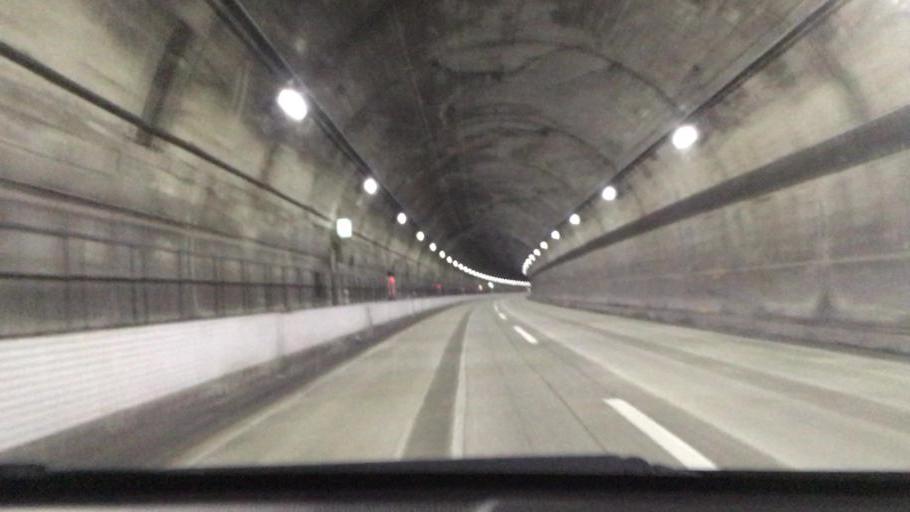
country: JP
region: Yamaguchi
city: Hofu
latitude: 34.0544
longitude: 131.6323
